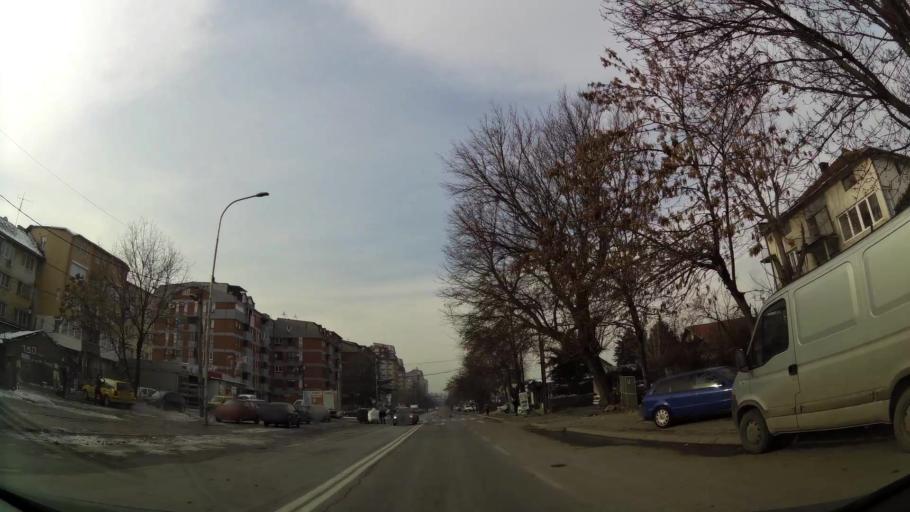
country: MK
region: Cair
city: Cair
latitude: 42.0137
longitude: 21.4410
